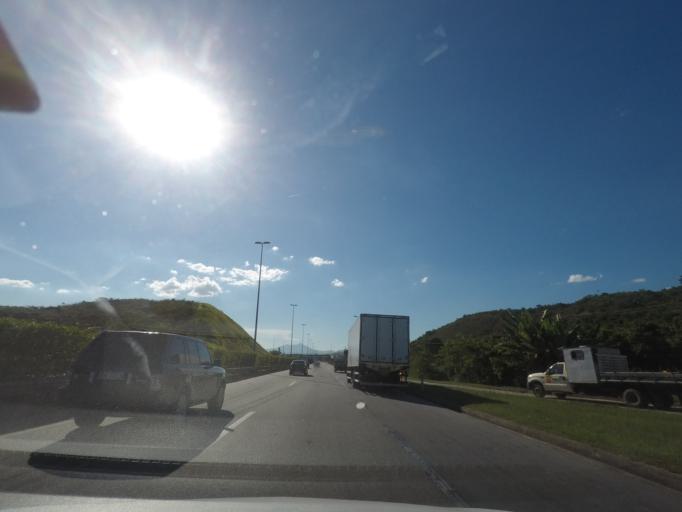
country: BR
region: Rio de Janeiro
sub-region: Petropolis
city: Petropolis
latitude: -22.6521
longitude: -43.1629
